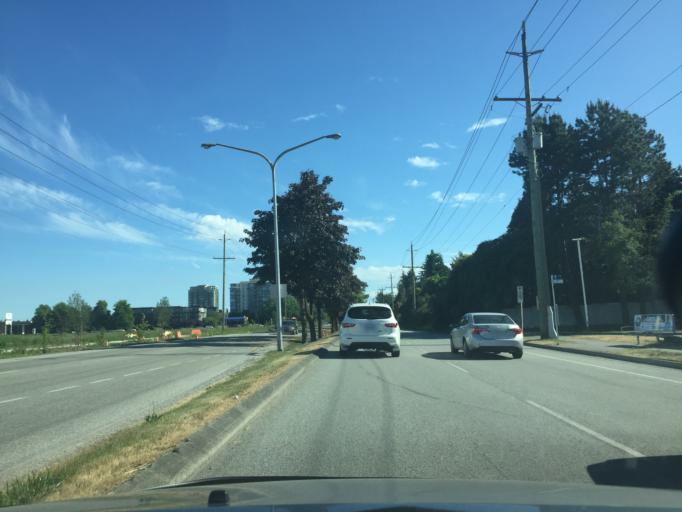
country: CA
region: British Columbia
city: Richmond
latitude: 49.1736
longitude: -123.1247
